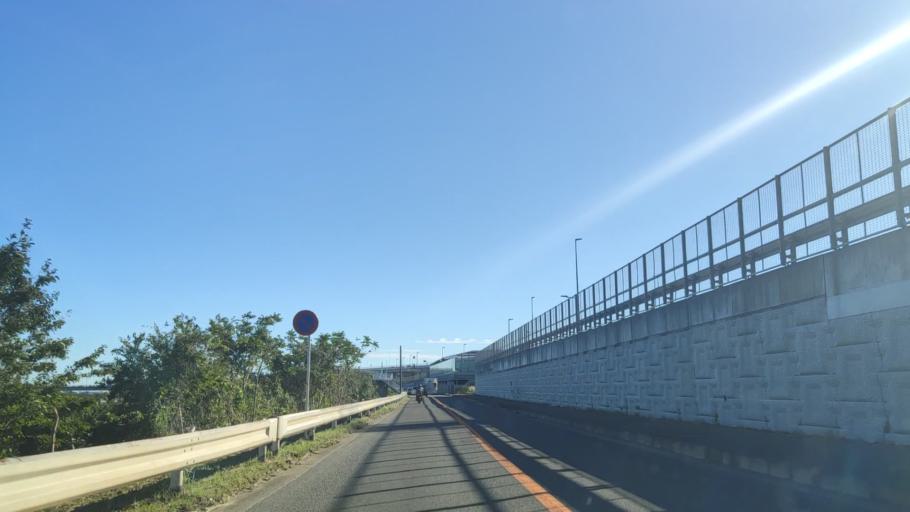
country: JP
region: Kanagawa
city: Zama
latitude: 35.4934
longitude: 139.3701
